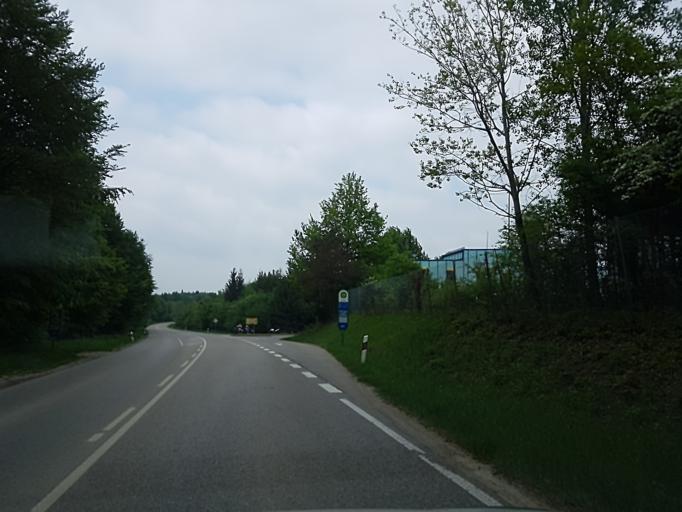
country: DE
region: Bavaria
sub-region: Upper Bavaria
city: Ebersberg
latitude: 48.1103
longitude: 11.9810
